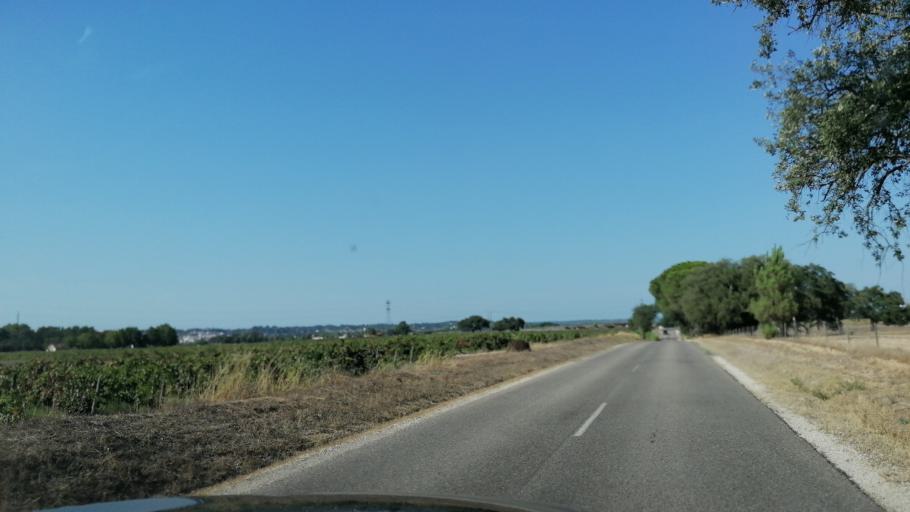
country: PT
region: Santarem
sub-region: Coruche
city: Coruche
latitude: 38.9314
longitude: -8.5196
